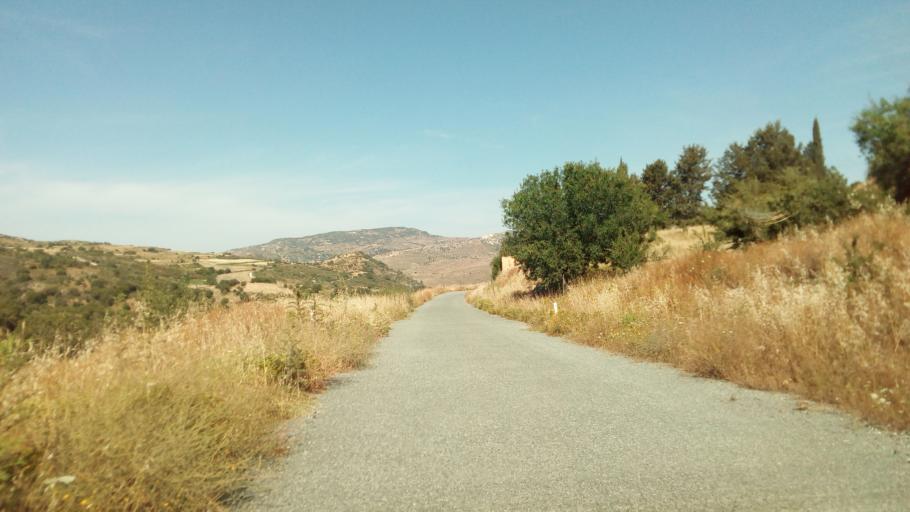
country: CY
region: Limassol
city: Pachna
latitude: 34.8131
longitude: 32.7393
